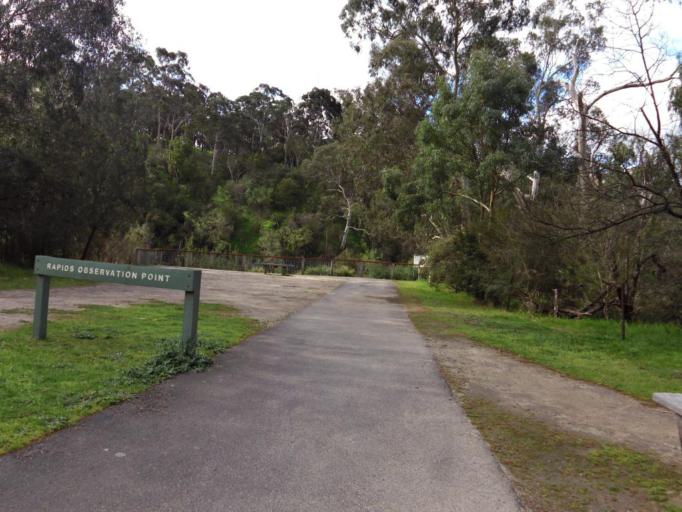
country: AU
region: Victoria
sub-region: Banyule
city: Lower Plenty
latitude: -37.7409
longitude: 145.1240
